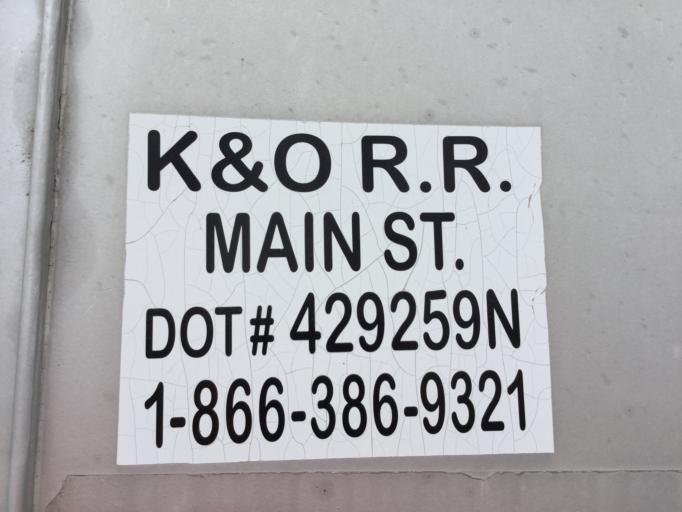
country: US
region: Kansas
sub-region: Barton County
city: Hoisington
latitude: 38.5113
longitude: -98.7776
